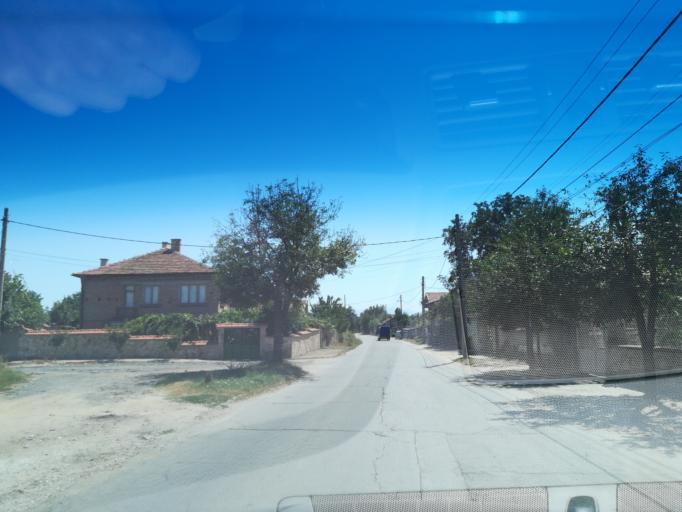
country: BG
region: Pazardzhik
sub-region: Obshtina Pazardzhik
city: Pazardzhik
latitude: 42.2791
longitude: 24.3950
